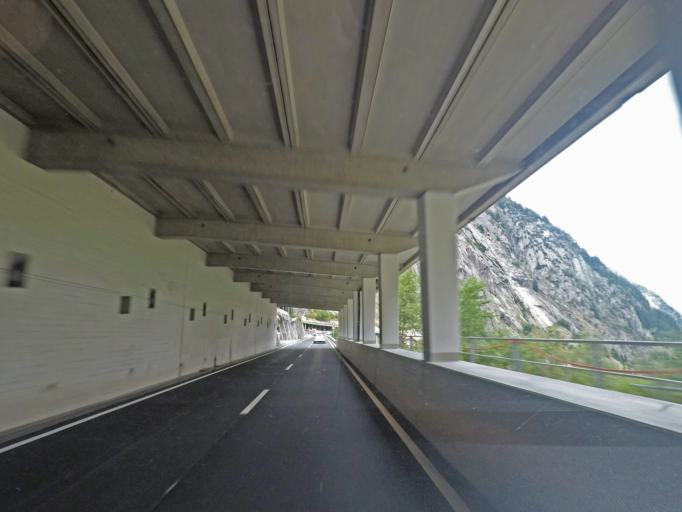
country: CH
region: Uri
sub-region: Uri
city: Andermatt
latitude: 46.6546
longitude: 8.5859
